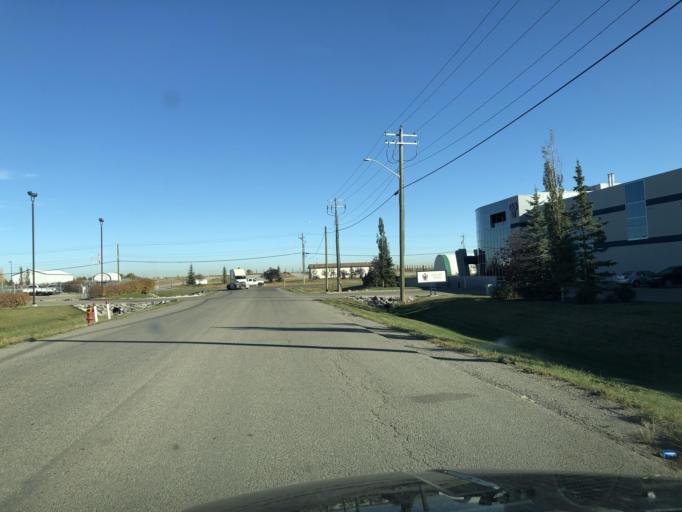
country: CA
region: Alberta
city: Chestermere
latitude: 50.9691
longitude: -113.9026
